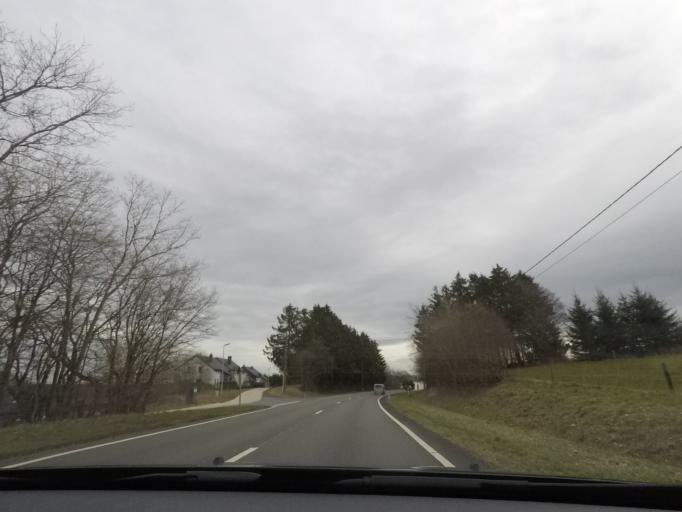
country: LU
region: Diekirch
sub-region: Canton de Wiltz
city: Winseler
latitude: 49.9849
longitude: 5.8292
